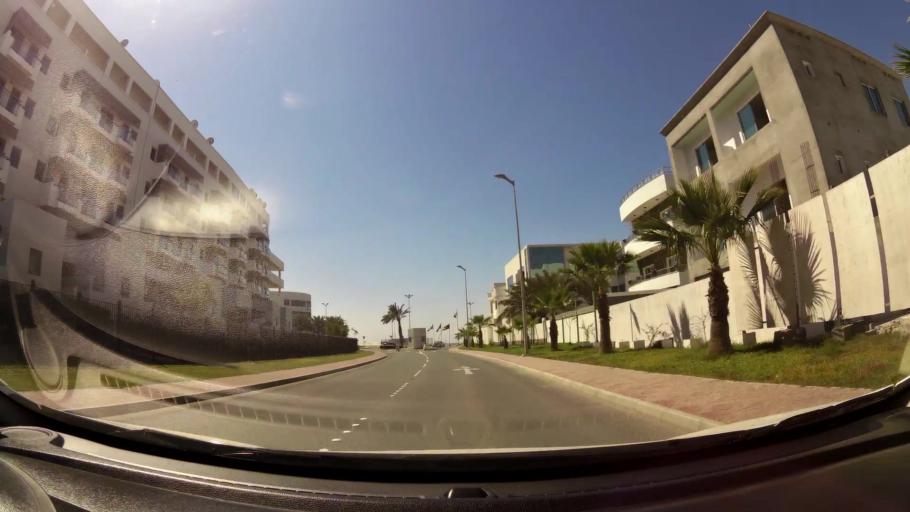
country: BH
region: Muharraq
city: Al Hadd
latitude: 26.3007
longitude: 50.6623
